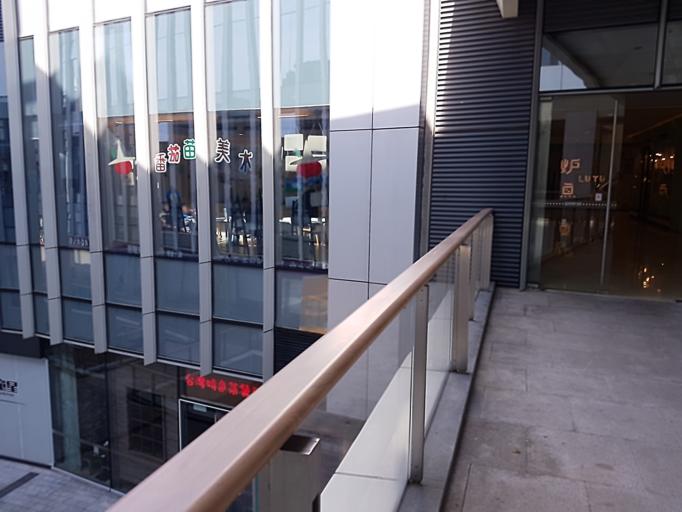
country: CN
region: Zhejiang Sheng
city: Gudang
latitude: 30.3014
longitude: 120.1032
